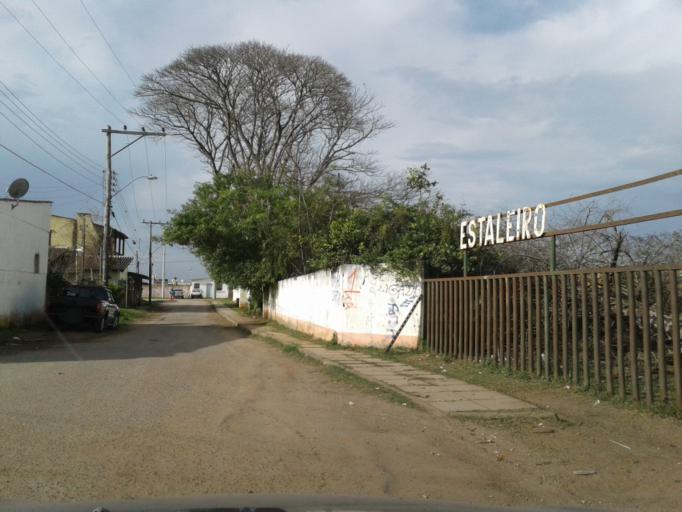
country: BR
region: Rio Grande do Sul
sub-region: Porto Alegre
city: Porto Alegre
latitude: -30.0296
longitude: -51.2526
